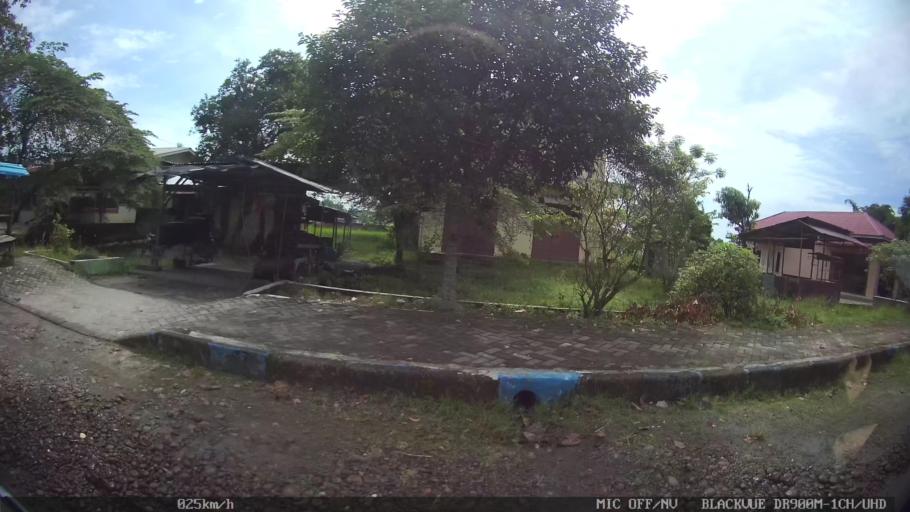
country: ID
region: North Sumatra
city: Percut
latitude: 3.5995
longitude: 98.8076
